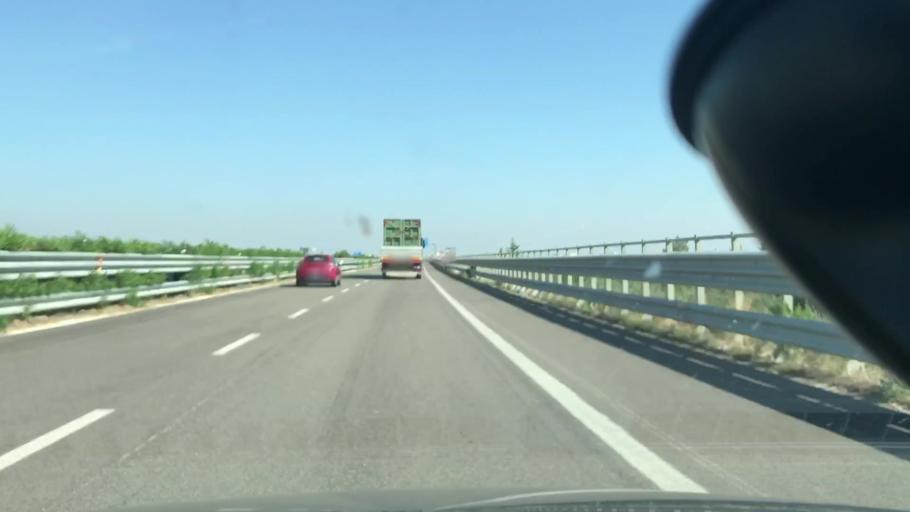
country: IT
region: Apulia
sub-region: Provincia di Foggia
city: Foggia
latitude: 41.4199
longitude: 15.5589
